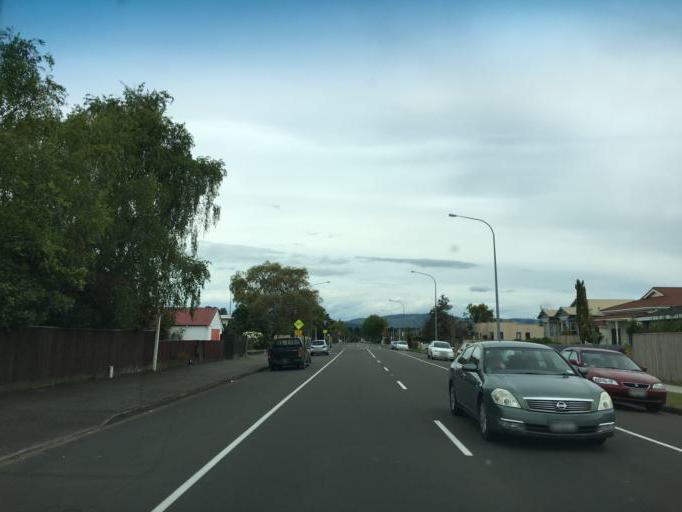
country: NZ
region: Manawatu-Wanganui
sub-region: Palmerston North City
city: Palmerston North
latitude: -40.3681
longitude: 175.5979
